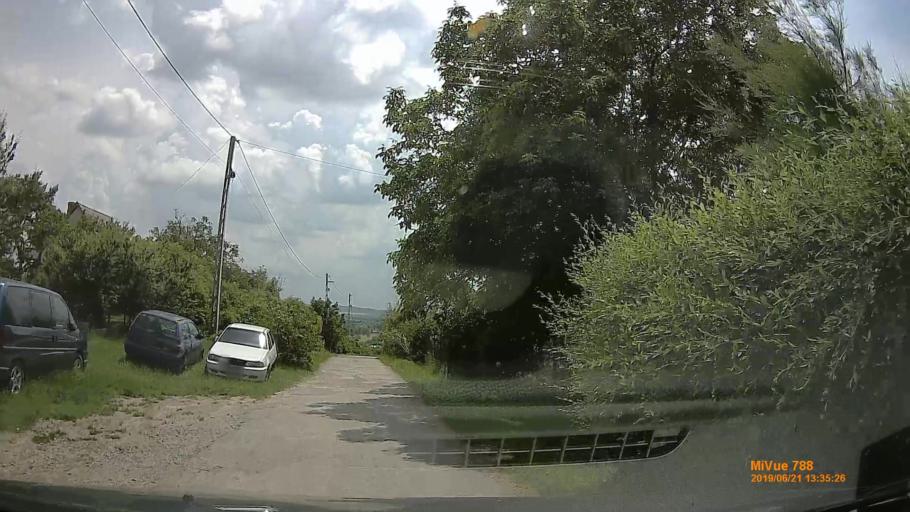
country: HU
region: Baranya
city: Pellerd
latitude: 46.0637
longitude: 18.1371
